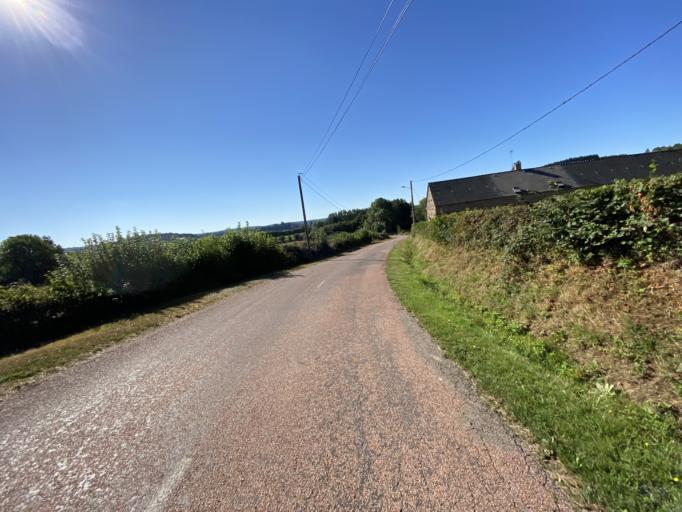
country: FR
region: Bourgogne
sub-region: Departement de la Cote-d'Or
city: Saulieu
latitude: 47.2692
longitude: 4.1741
